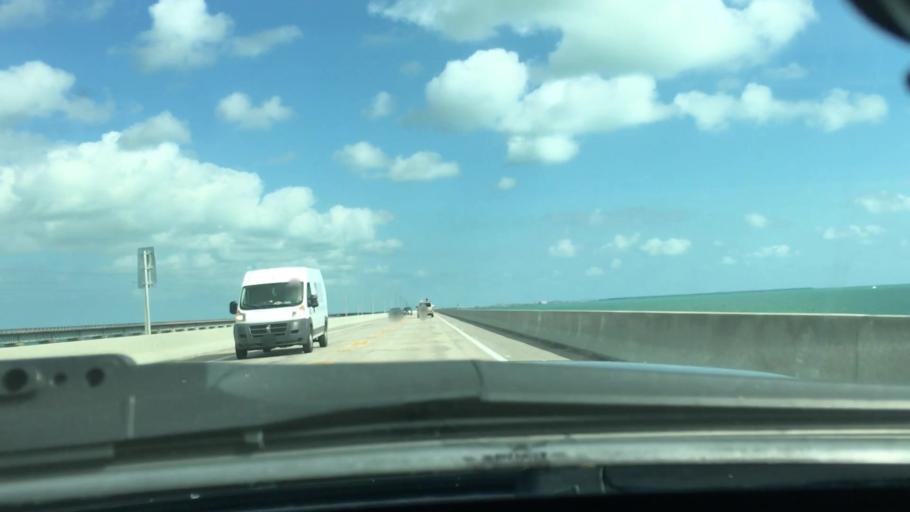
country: US
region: Florida
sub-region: Monroe County
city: Marathon
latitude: 24.6951
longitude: -81.1831
